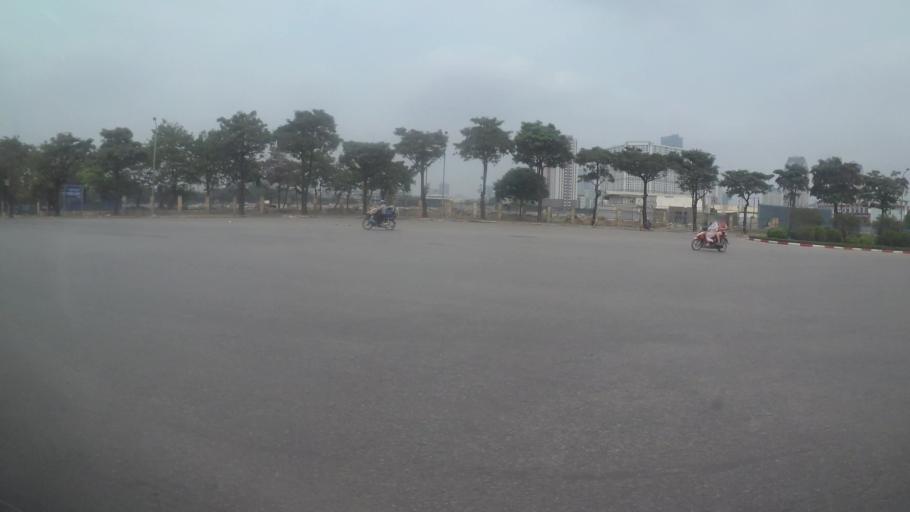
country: VN
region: Ha Noi
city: Cau Dien
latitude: 21.0177
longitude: 105.7671
